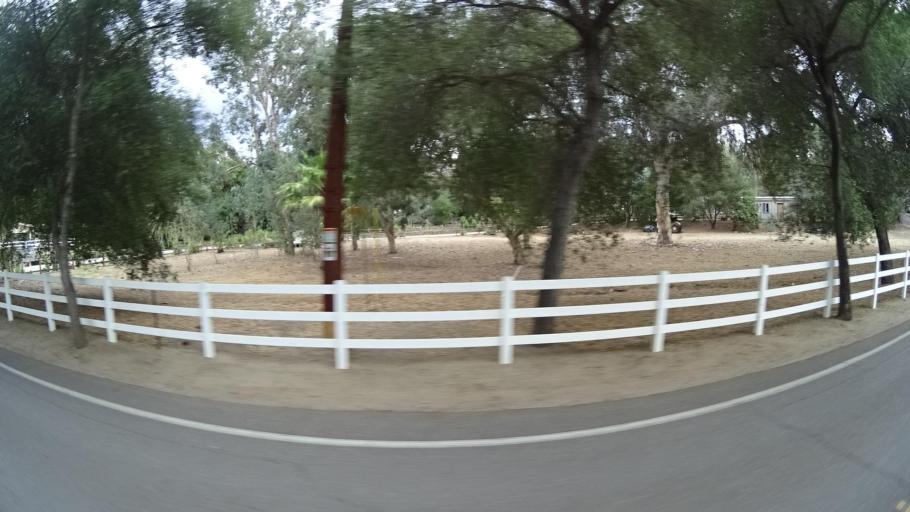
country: US
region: California
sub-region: San Diego County
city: Ramona
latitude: 32.9704
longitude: -116.9141
